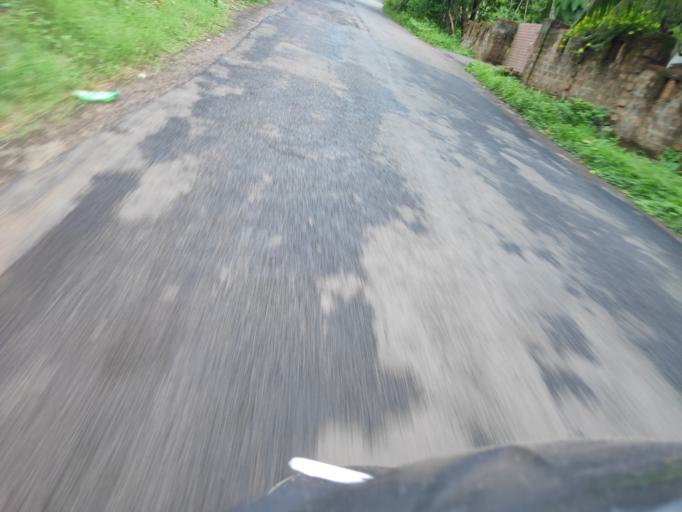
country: IN
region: Kerala
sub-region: Malappuram
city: Manjeri
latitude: 11.1785
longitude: 76.1953
